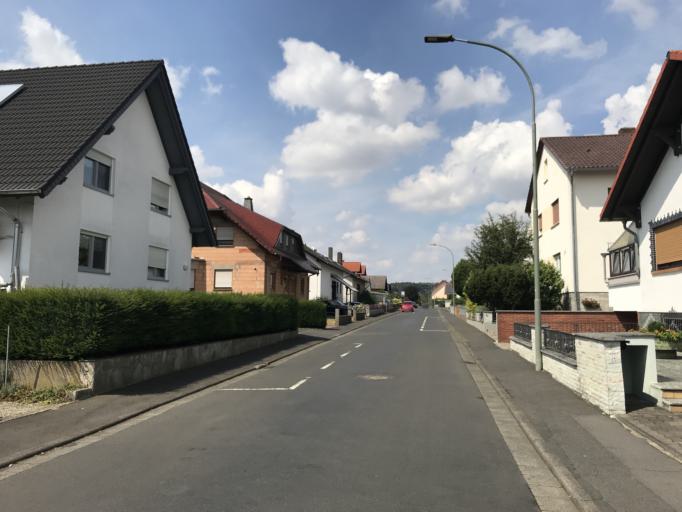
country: DE
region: Hesse
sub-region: Regierungsbezirk Darmstadt
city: Wolfersheim
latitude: 50.4475
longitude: 8.8428
